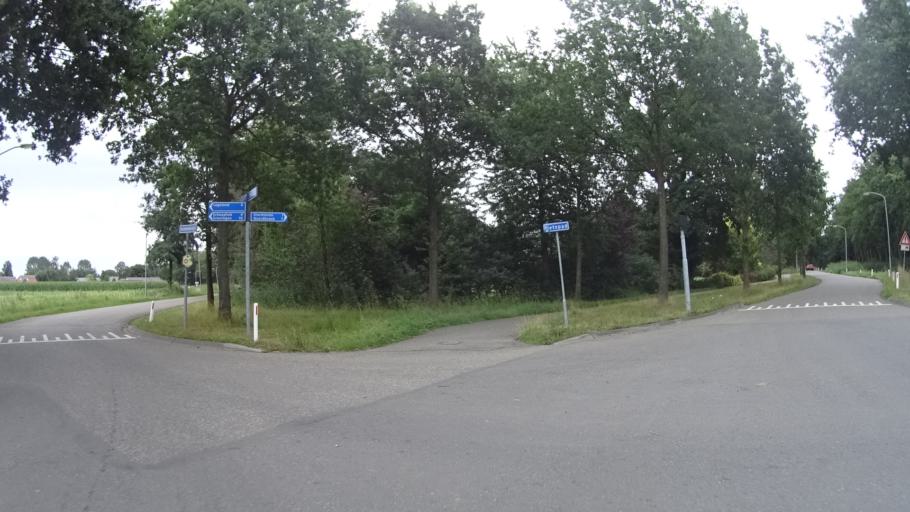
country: NL
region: Groningen
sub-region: Gemeente Slochteren
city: Slochteren
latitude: 53.2234
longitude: 6.7934
